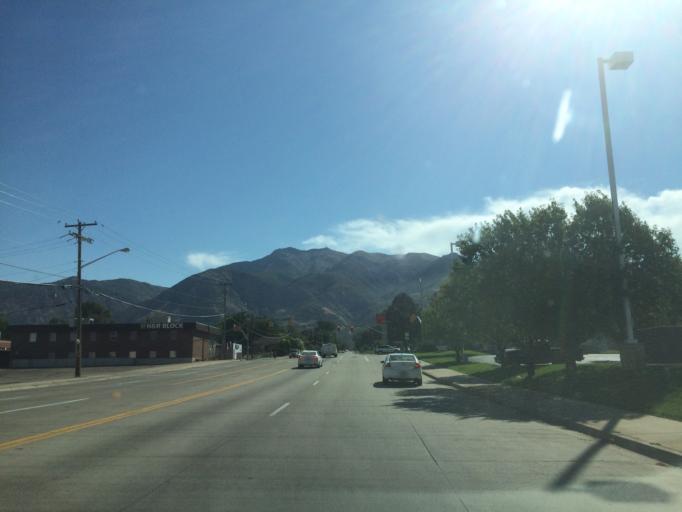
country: US
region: Utah
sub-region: Weber County
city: South Ogden
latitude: 41.1978
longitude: -111.9725
